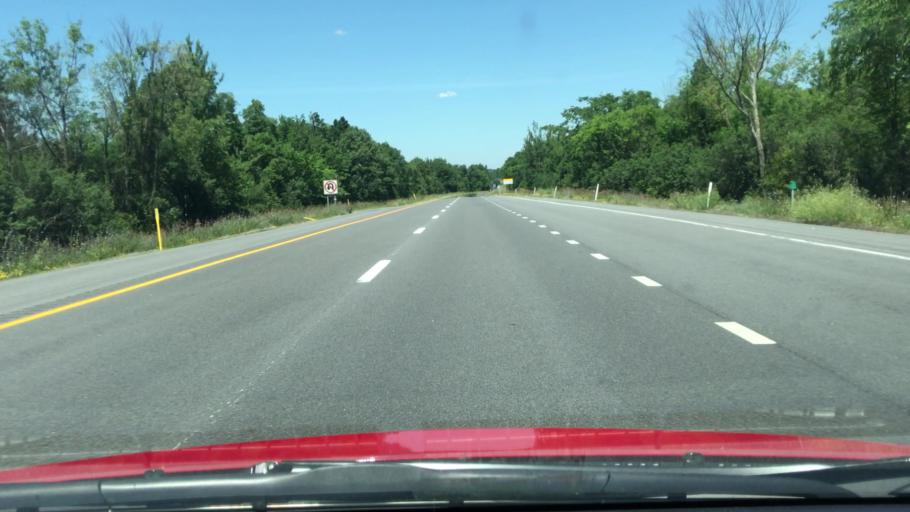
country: US
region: New York
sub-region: Clinton County
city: Cumberland Head
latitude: 44.8102
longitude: -73.4453
